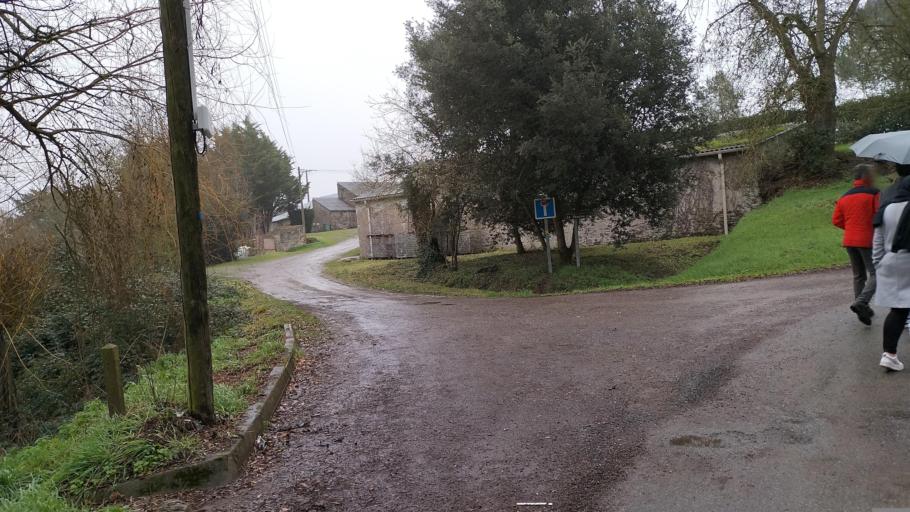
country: FR
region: Pays de la Loire
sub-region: Departement de Maine-et-Loire
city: La Pommeraye
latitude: 47.3628
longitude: -0.8545
